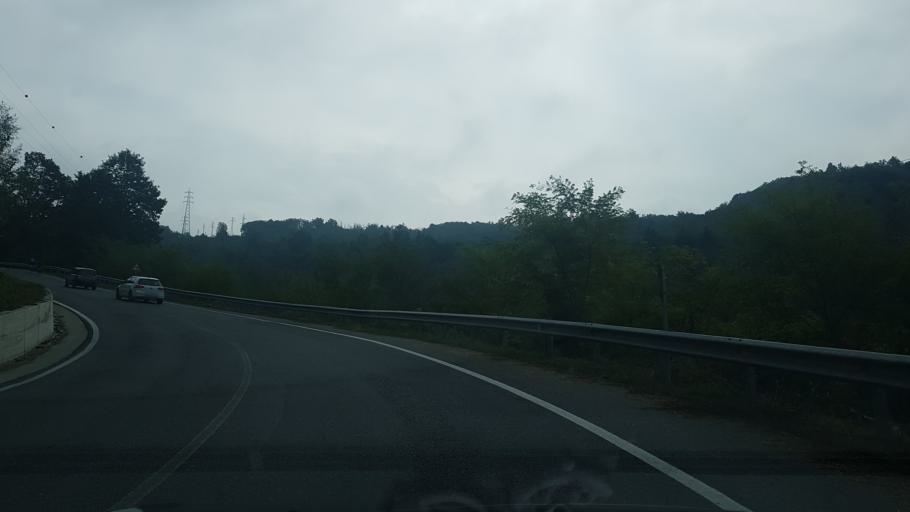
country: IT
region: Piedmont
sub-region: Provincia di Cuneo
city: Sale delle Langhe
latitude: 44.4006
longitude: 8.1079
